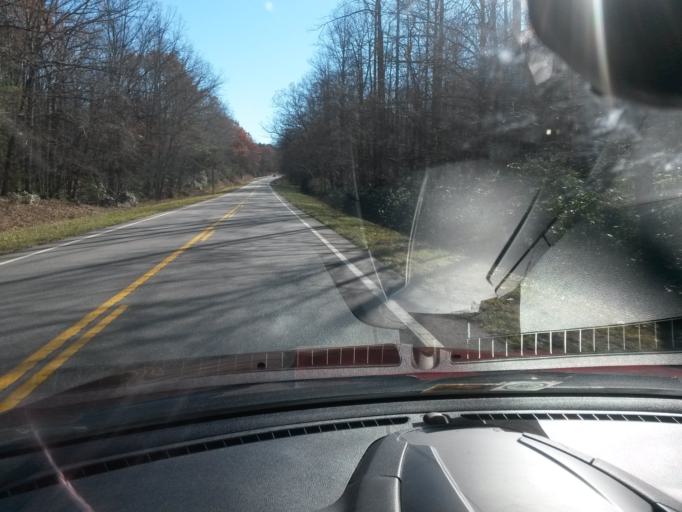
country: US
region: Virginia
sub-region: Henry County
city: Pannill Fork
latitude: 36.7653
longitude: -80.0990
